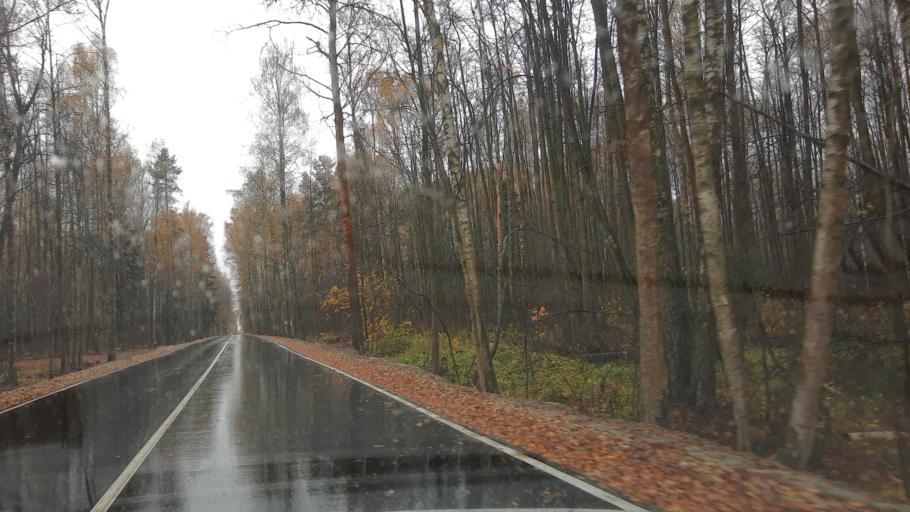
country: RU
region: Moskovskaya
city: Imeni Vorovskogo
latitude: 55.7930
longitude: 38.3684
